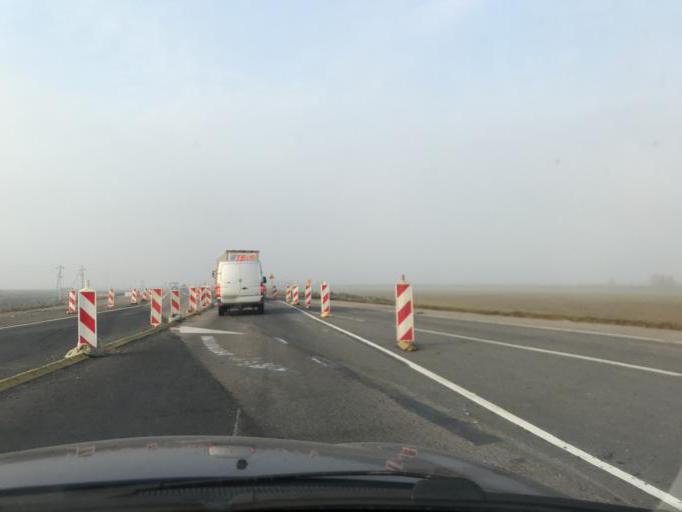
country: BY
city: Berezovka
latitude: 53.8386
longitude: 25.4743
